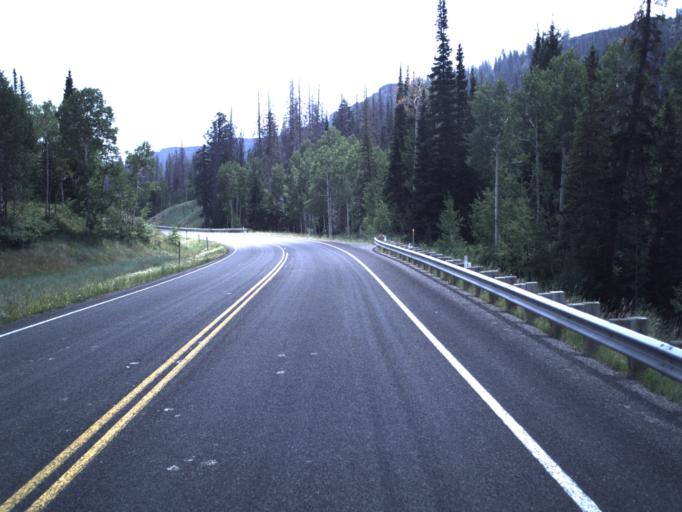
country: US
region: Utah
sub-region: Summit County
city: Francis
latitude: 40.4856
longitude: -110.9539
